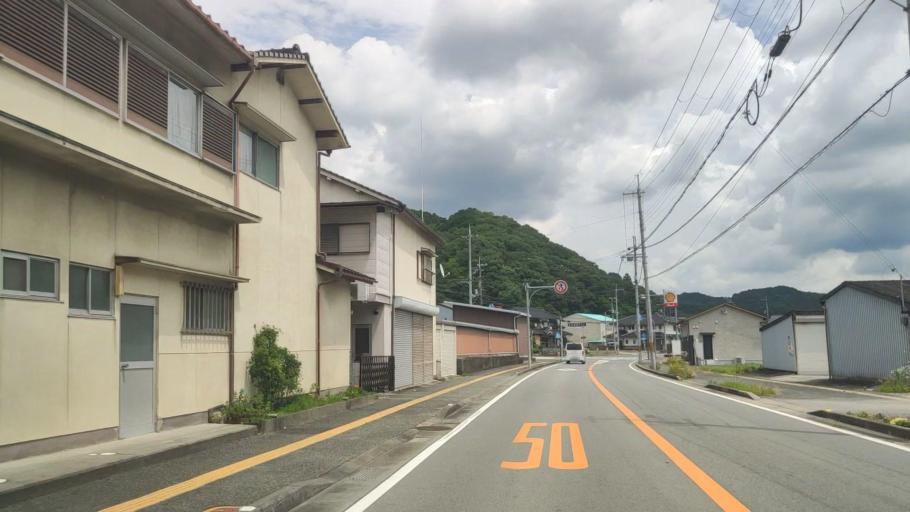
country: JP
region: Hyogo
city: Yamazakicho-nakabirose
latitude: 34.9843
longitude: 134.4373
